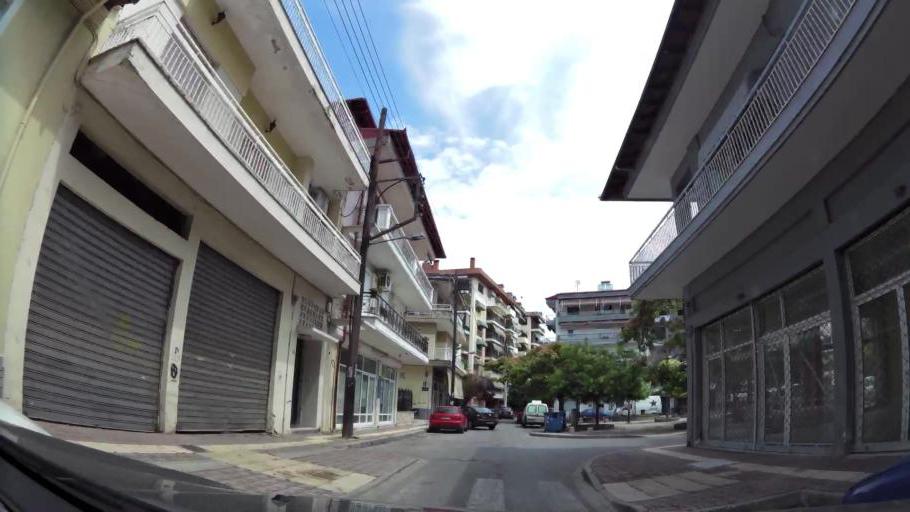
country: GR
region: Central Macedonia
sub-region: Nomos Pierias
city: Katerini
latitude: 40.2749
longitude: 22.5046
